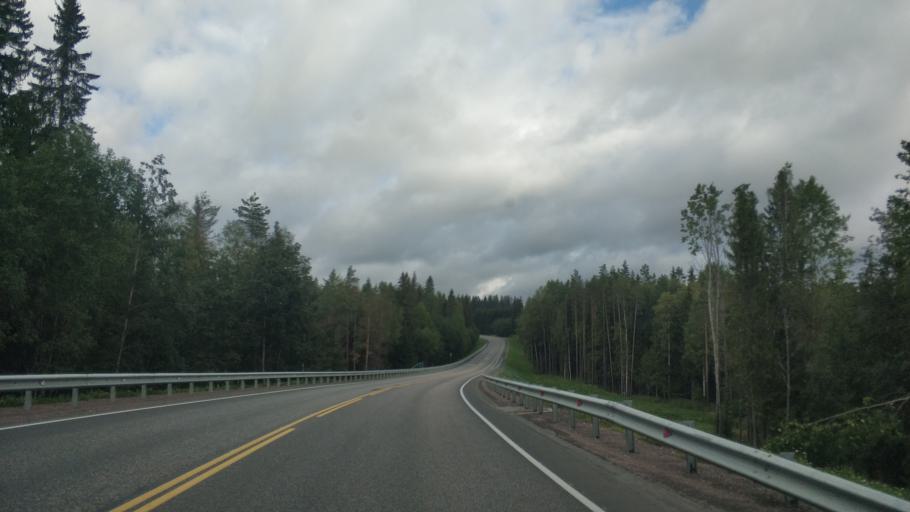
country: RU
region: Republic of Karelia
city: Khelyulya
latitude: 61.7882
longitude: 30.6337
